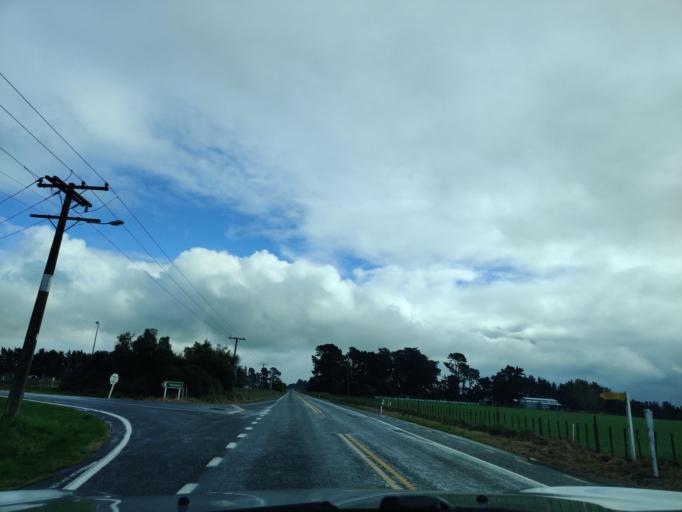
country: NZ
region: Hawke's Bay
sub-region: Hastings District
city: Hastings
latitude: -40.0175
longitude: 176.3510
